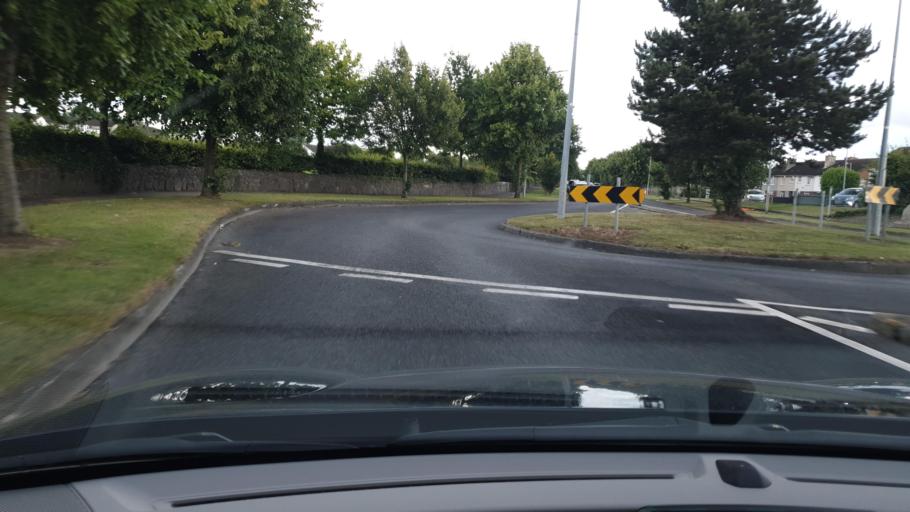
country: IE
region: Leinster
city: Clondalkin
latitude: 53.3266
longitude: -6.4252
